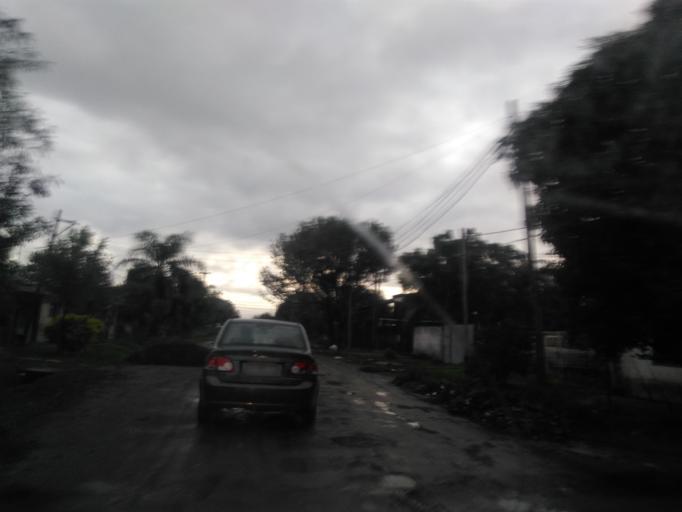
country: AR
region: Chaco
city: Resistencia
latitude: -27.4664
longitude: -59.0000
